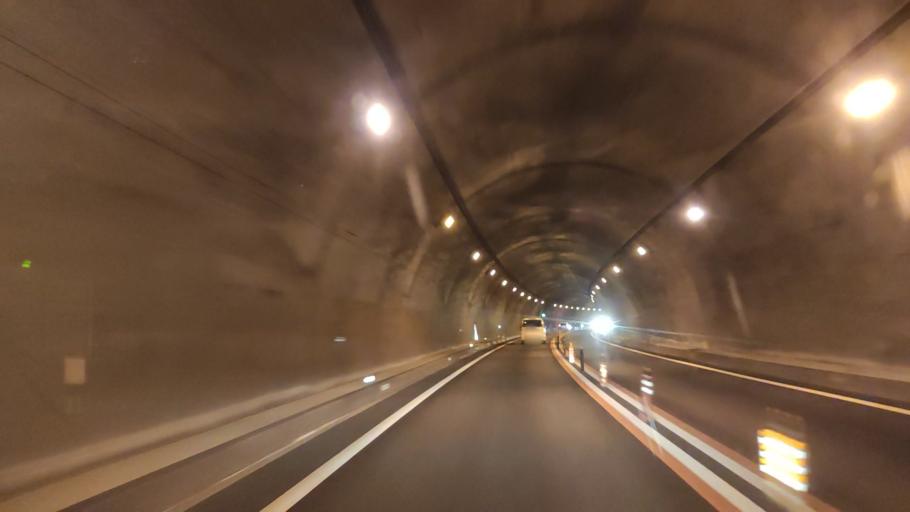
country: JP
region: Ehime
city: Kawanoecho
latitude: 33.9960
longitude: 133.6367
